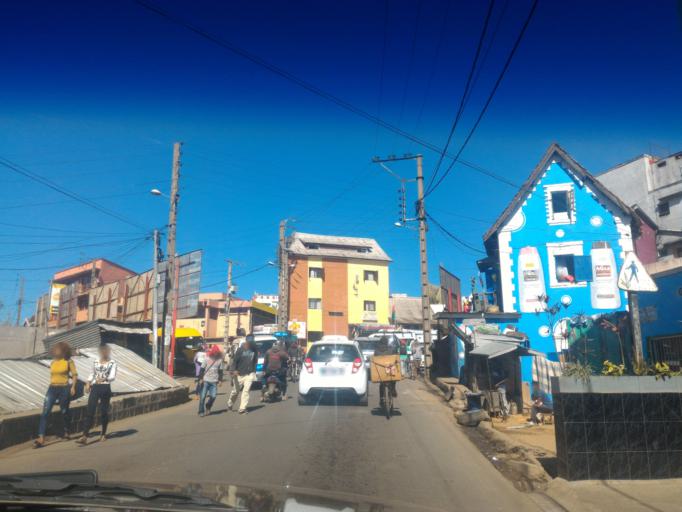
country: MG
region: Analamanga
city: Antananarivo
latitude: -18.9183
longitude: 47.5394
